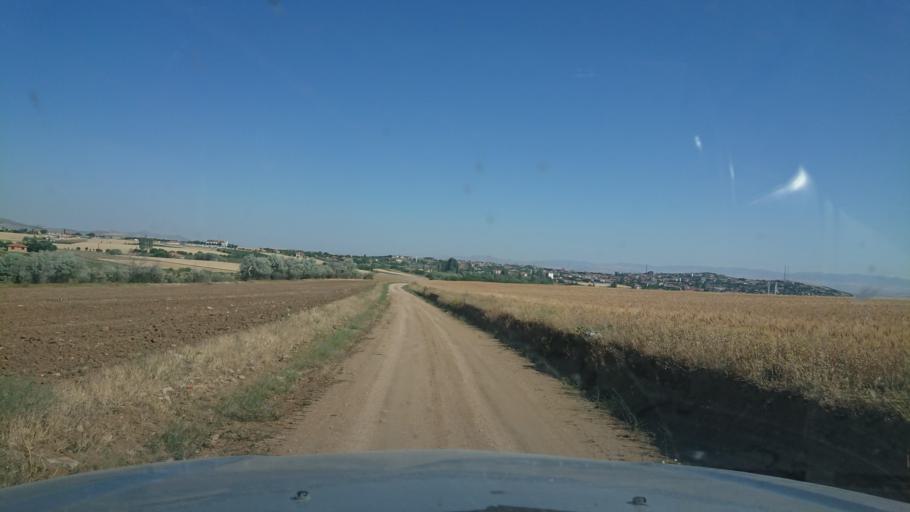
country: TR
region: Aksaray
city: Agacoren
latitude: 38.8542
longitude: 33.9145
